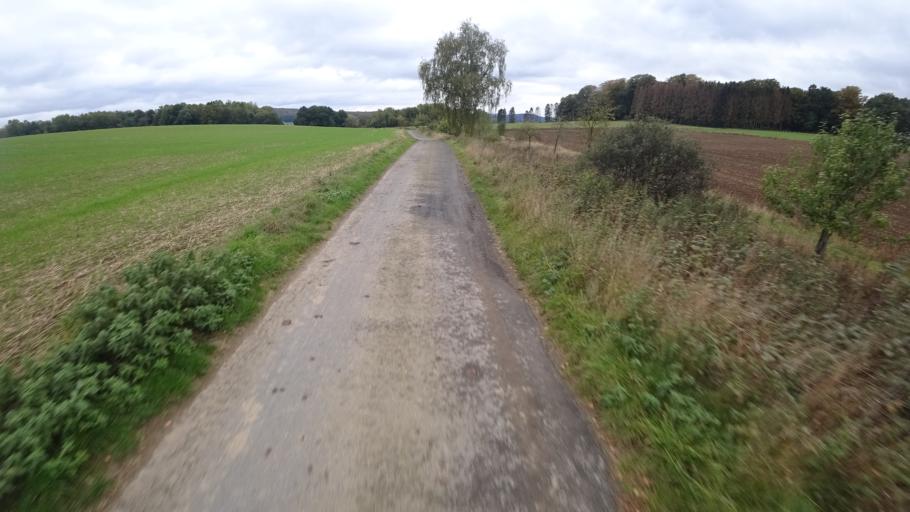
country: DE
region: Rheinland-Pfalz
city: Maxsain
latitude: 50.5558
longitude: 7.7786
